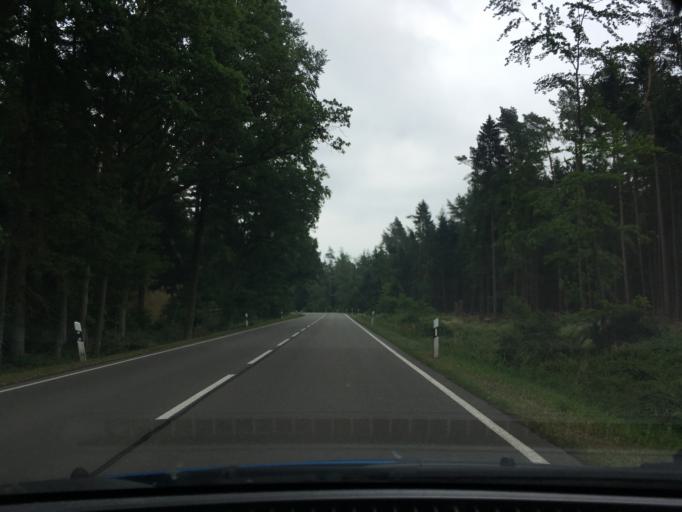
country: DE
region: Lower Saxony
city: Zernien
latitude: 53.0691
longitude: 10.9187
